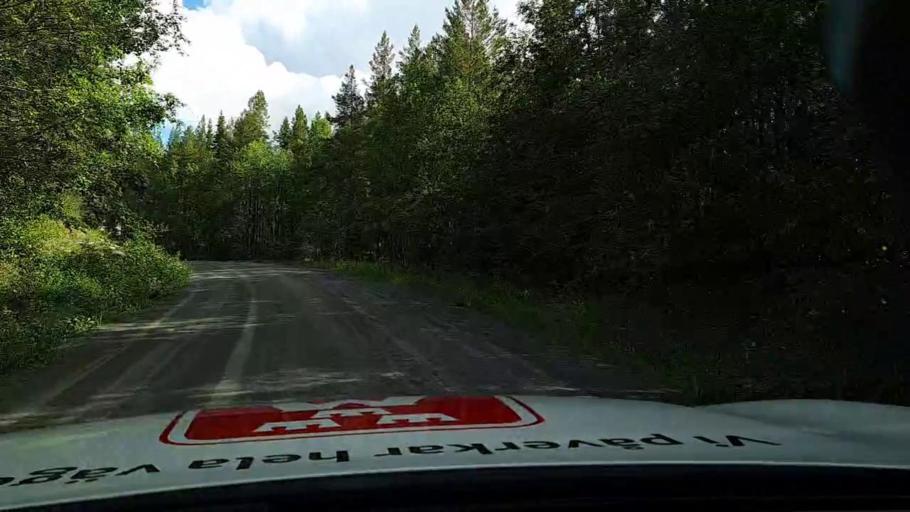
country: SE
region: Jaemtland
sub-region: OEstersunds Kommun
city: Brunflo
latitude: 63.1142
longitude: 15.0838
